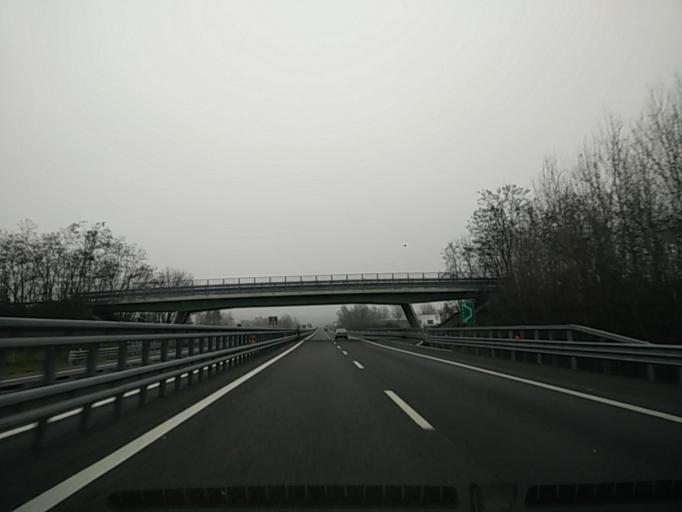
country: IT
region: Piedmont
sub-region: Provincia di Asti
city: Baldichieri d'Asti
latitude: 44.9030
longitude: 8.0785
